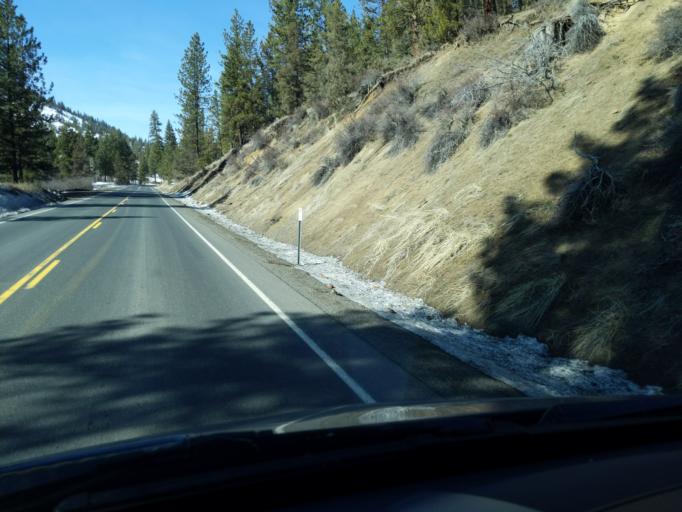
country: US
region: Oregon
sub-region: Grant County
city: John Day
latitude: 44.8913
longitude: -119.0120
